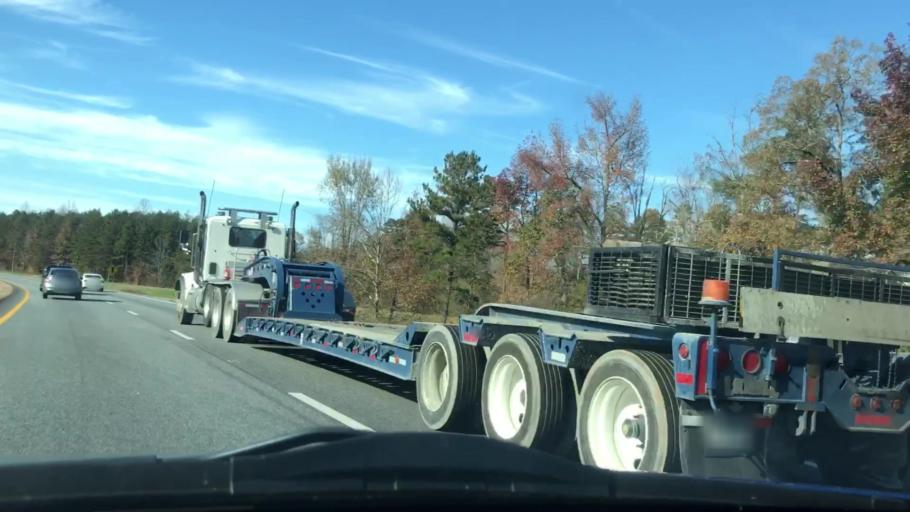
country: US
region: North Carolina
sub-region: Guilford County
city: High Point
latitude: 36.0135
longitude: -80.0371
